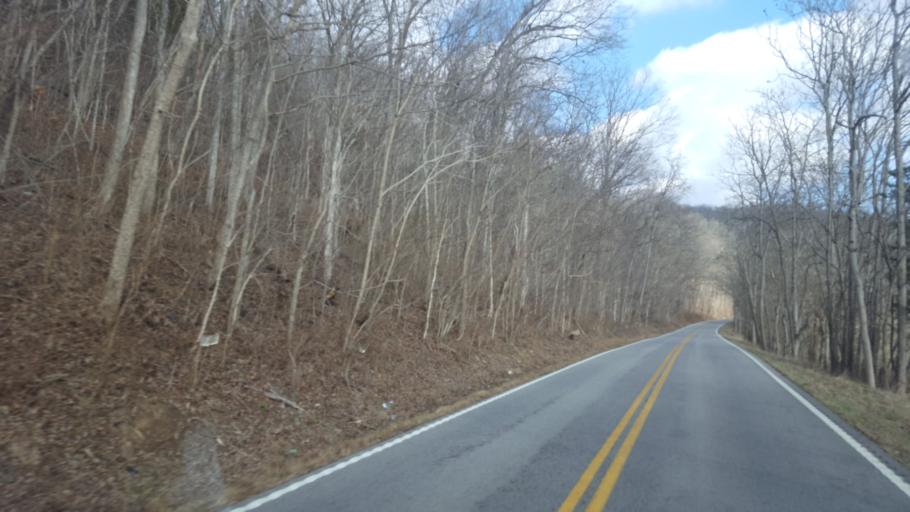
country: US
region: Kentucky
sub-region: Owen County
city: Owenton
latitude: 38.4382
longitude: -84.8864
